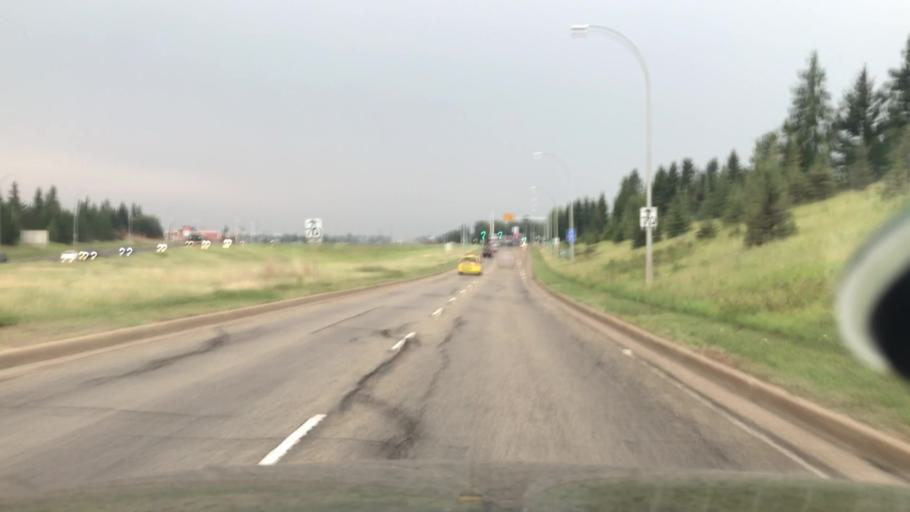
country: CA
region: Alberta
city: Edmonton
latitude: 53.4793
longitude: -113.5731
